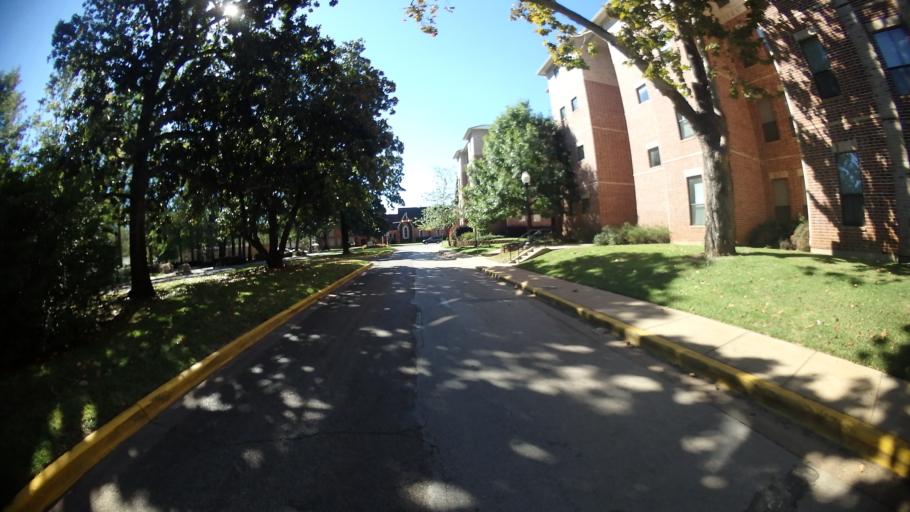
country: US
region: Texas
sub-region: Nacogdoches County
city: Nacogdoches
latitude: 31.6168
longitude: -94.6491
